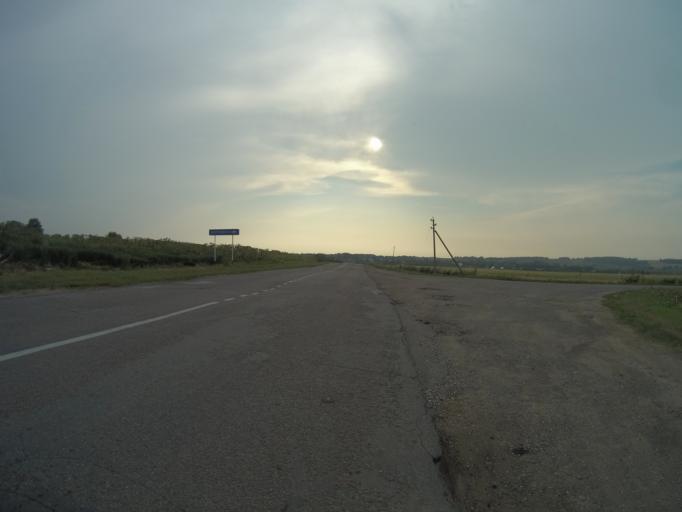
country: RU
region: Ivanovo
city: Gavrilov Posad
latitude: 56.3463
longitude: 40.1634
